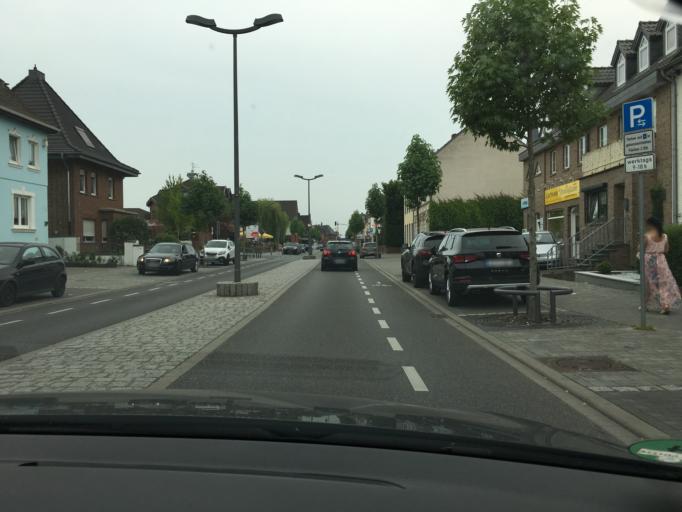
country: DE
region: North Rhine-Westphalia
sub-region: Regierungsbezirk Koln
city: Kerpen
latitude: 50.8722
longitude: 6.6930
